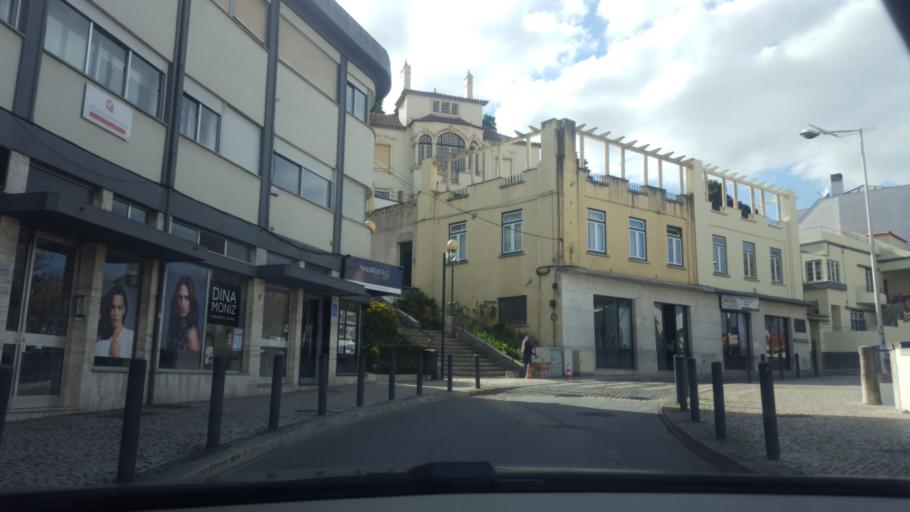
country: PT
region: Leiria
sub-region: Leiria
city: Leiria
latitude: 39.7425
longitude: -8.8076
